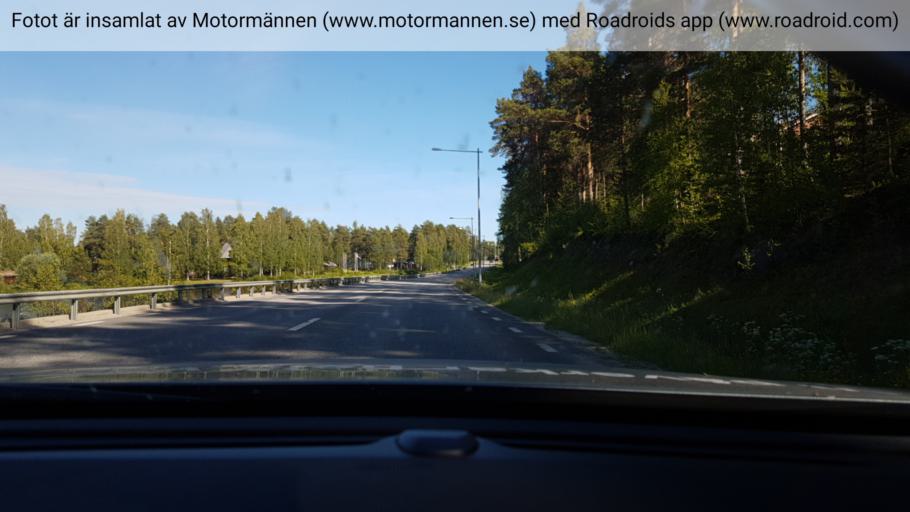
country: SE
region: Vaesterbotten
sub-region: Lycksele Kommun
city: Lycksele
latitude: 64.6059
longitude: 18.6609
